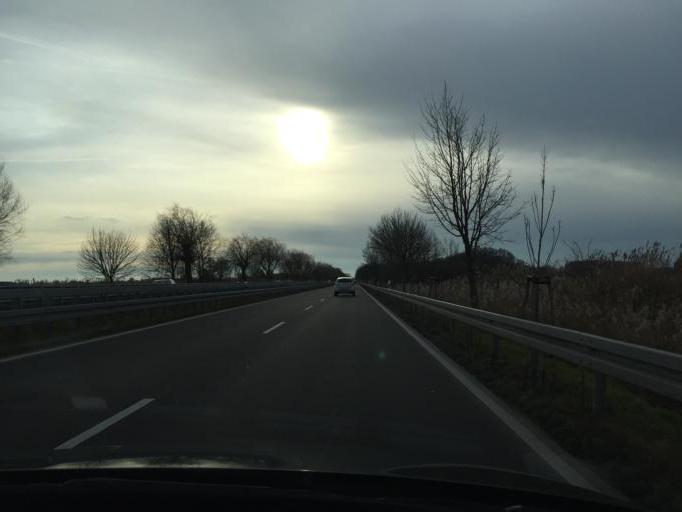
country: DE
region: Brandenburg
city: Peitz
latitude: 51.8431
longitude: 14.3879
